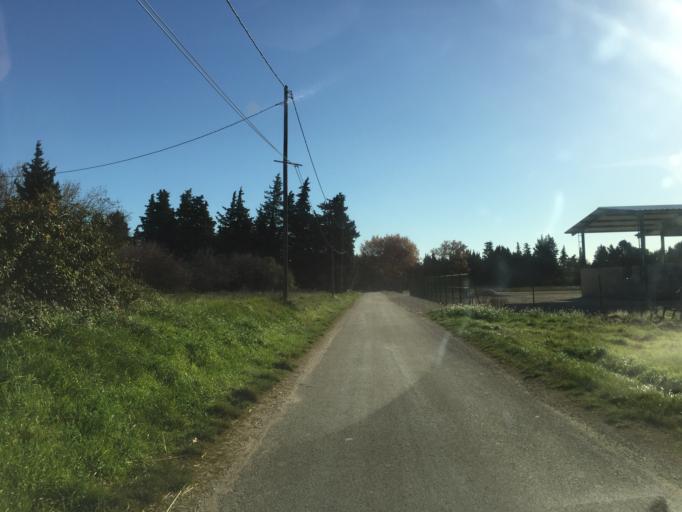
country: FR
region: Provence-Alpes-Cote d'Azur
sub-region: Departement du Vaucluse
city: Courthezon
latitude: 44.0808
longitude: 4.9108
